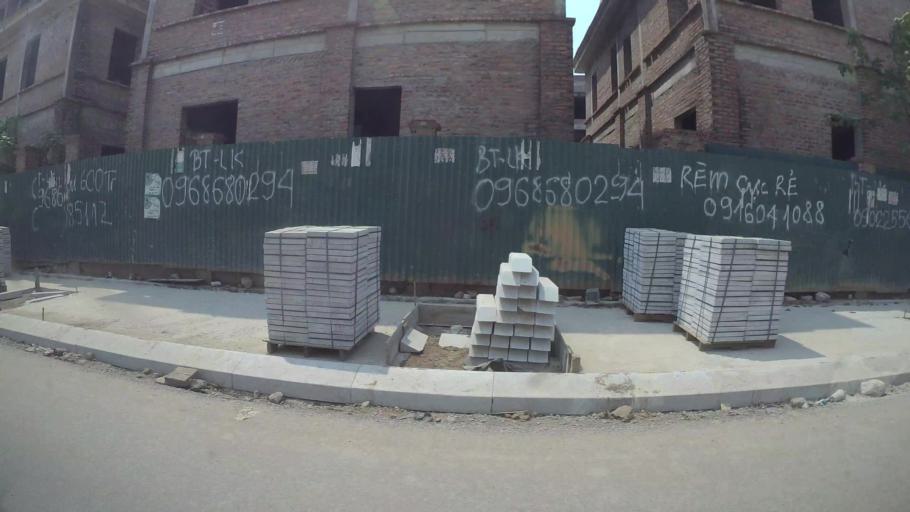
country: VN
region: Ha Noi
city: Ha Dong
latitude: 20.9937
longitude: 105.7611
